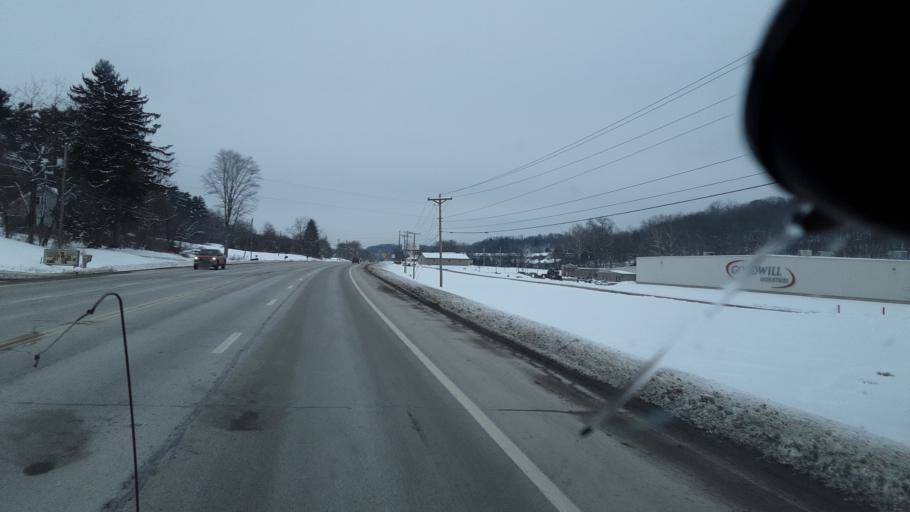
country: US
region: Ohio
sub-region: Muskingum County
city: Zanesville
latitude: 39.9545
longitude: -82.0685
